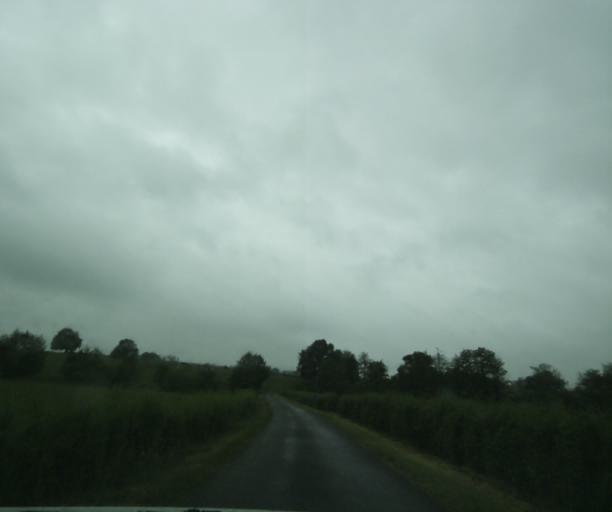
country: FR
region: Bourgogne
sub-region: Departement de Saone-et-Loire
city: Palinges
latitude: 46.4894
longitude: 4.1950
